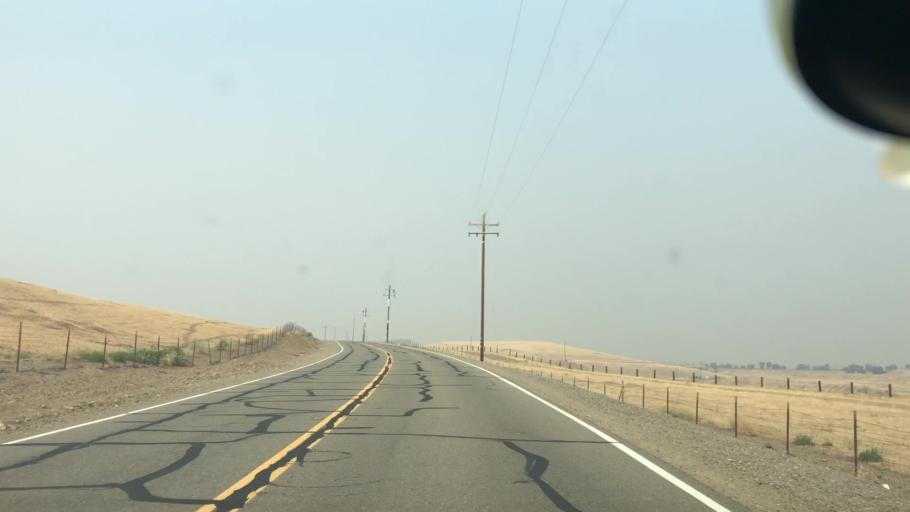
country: US
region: California
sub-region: San Joaquin County
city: Tracy
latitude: 37.6640
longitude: -121.4666
